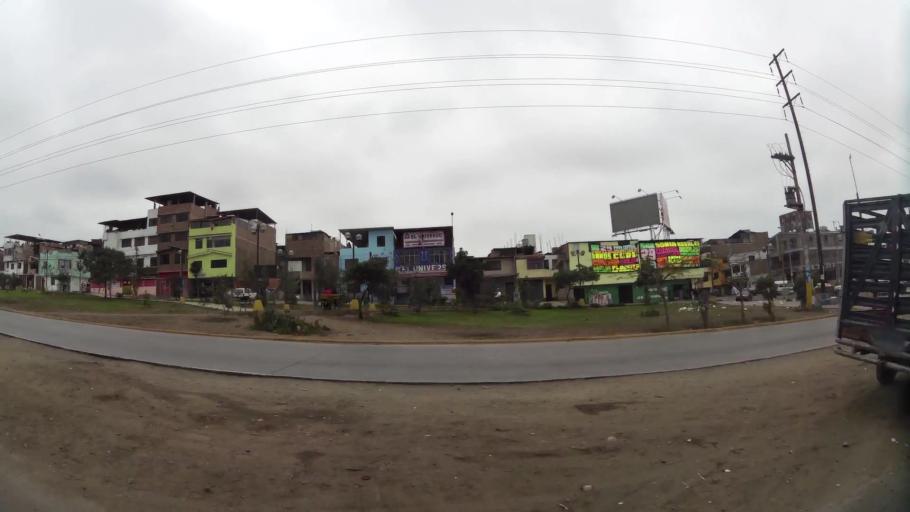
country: PE
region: Lima
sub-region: Lima
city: Surco
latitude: -12.1956
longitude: -76.9535
